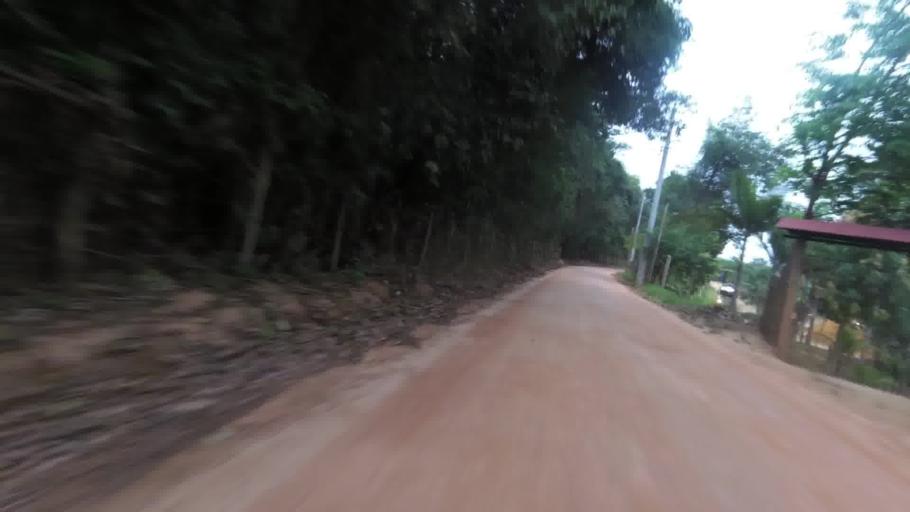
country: BR
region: Espirito Santo
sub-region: Alfredo Chaves
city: Alfredo Chaves
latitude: -20.6906
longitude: -40.7106
